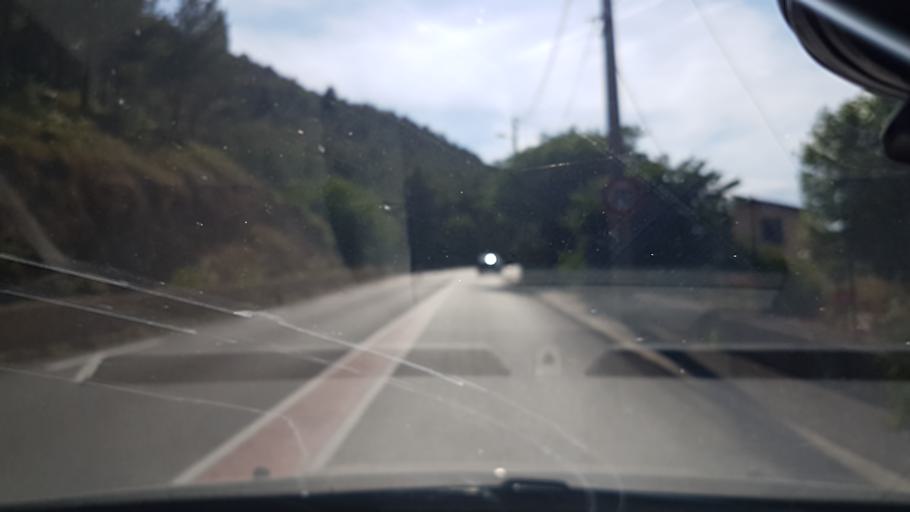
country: FR
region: Provence-Alpes-Cote d'Azur
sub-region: Departement des Bouches-du-Rhone
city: Marseille 11
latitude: 43.2466
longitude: 5.4560
